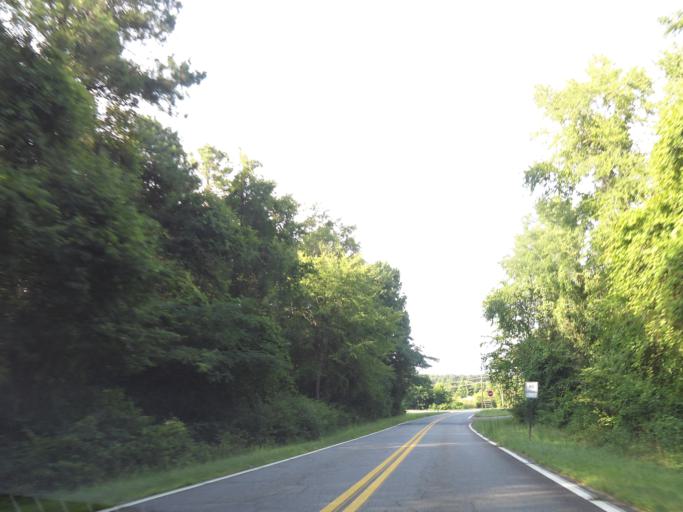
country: US
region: Georgia
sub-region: Houston County
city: Centerville
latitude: 32.7111
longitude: -83.6603
